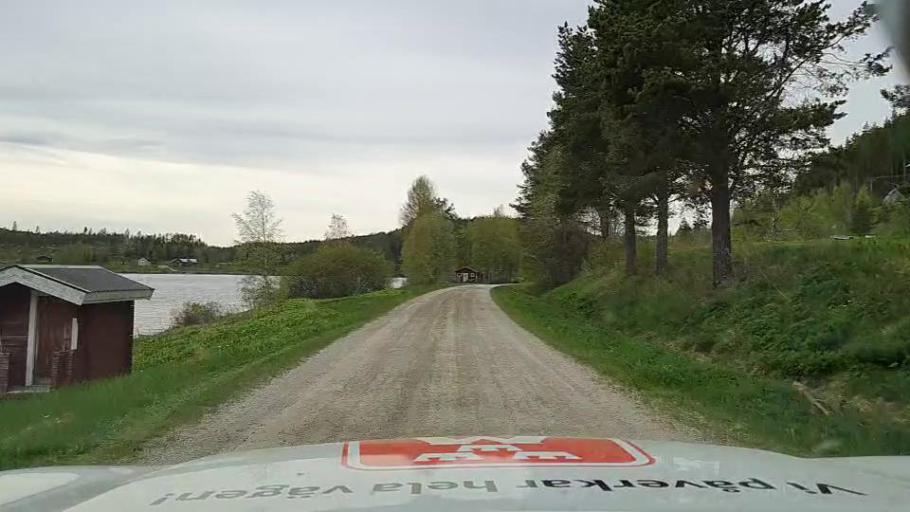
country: SE
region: Jaemtland
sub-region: Bergs Kommun
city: Hoverberg
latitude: 62.6860
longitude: 14.7879
